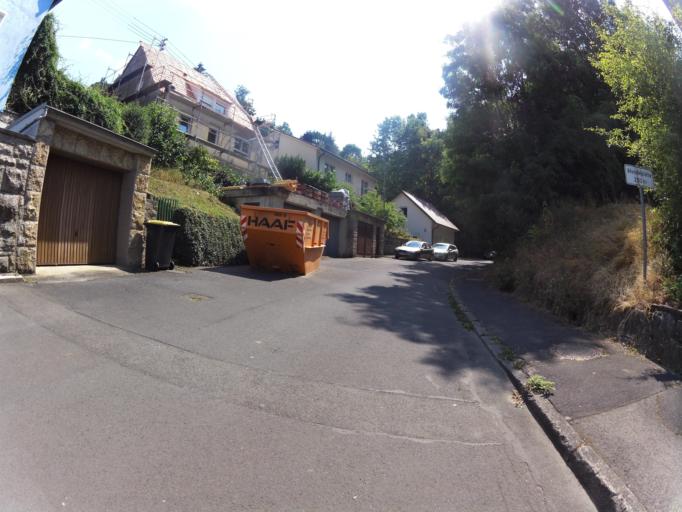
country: DE
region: Bavaria
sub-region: Regierungsbezirk Unterfranken
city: Ochsenfurt
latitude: 49.6586
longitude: 10.0600
